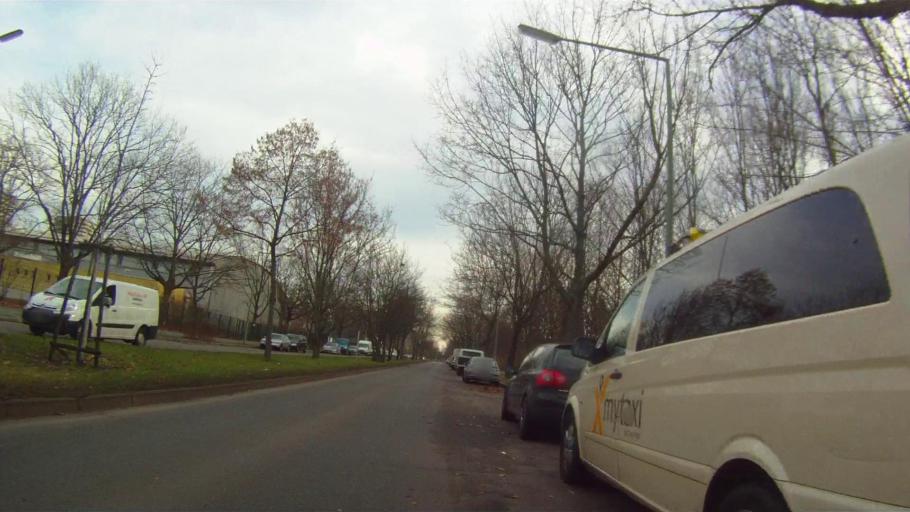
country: DE
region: Berlin
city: Buckow
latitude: 52.4237
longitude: 13.4531
